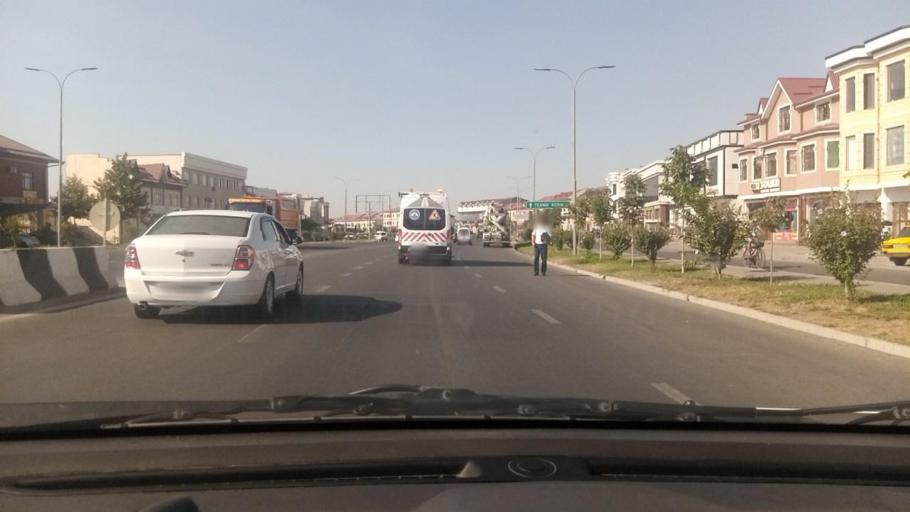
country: UZ
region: Toshkent Shahri
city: Bektemir
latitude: 41.2255
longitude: 69.3351
